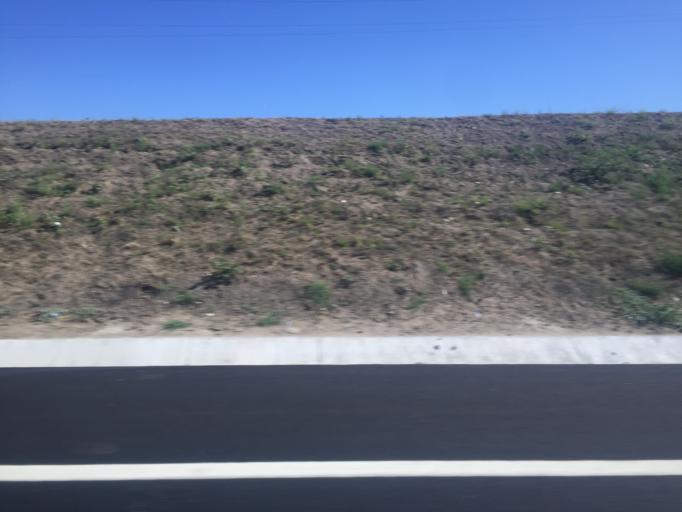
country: TR
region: Bursa
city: Gorukle
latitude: 40.2532
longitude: 28.7437
